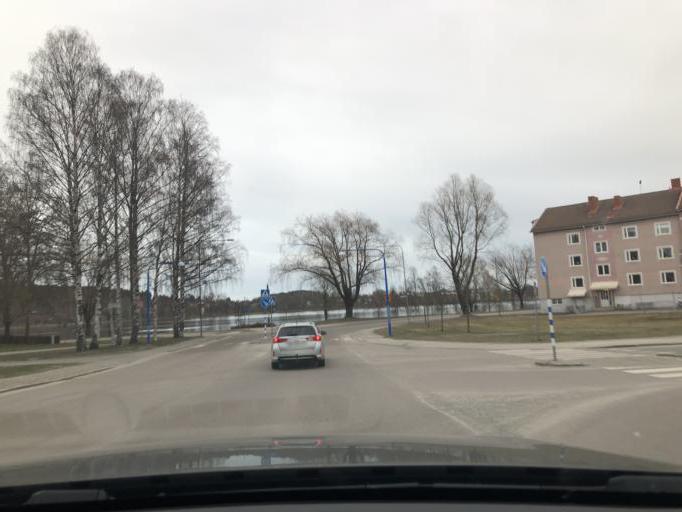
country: SE
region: Gaevleborg
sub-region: Hudiksvalls Kommun
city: Hudiksvall
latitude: 61.7339
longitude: 17.1020
